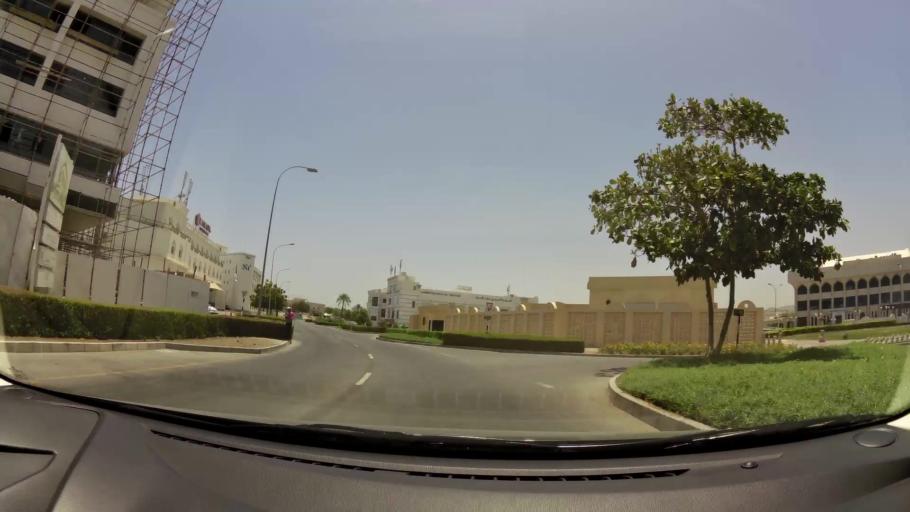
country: OM
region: Muhafazat Masqat
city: Bawshar
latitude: 23.6084
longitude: 58.4534
